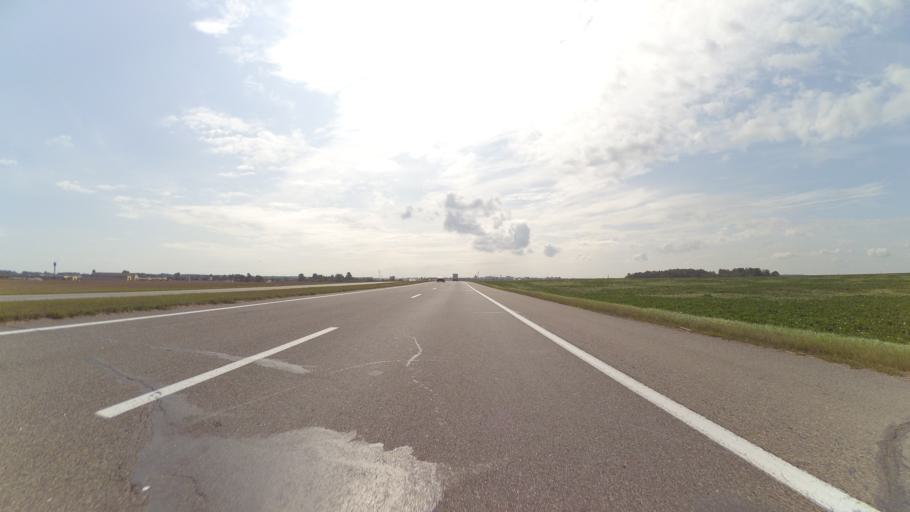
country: BY
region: Grodnenskaya
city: Skidal'
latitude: 53.6219
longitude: 24.0568
